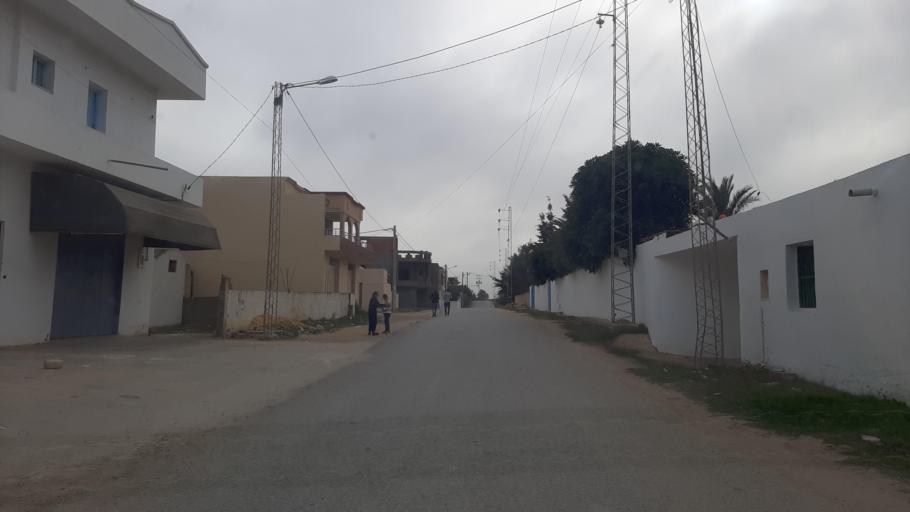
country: TN
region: Nabul
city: Menzel Heurr
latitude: 36.6789
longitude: 10.9243
